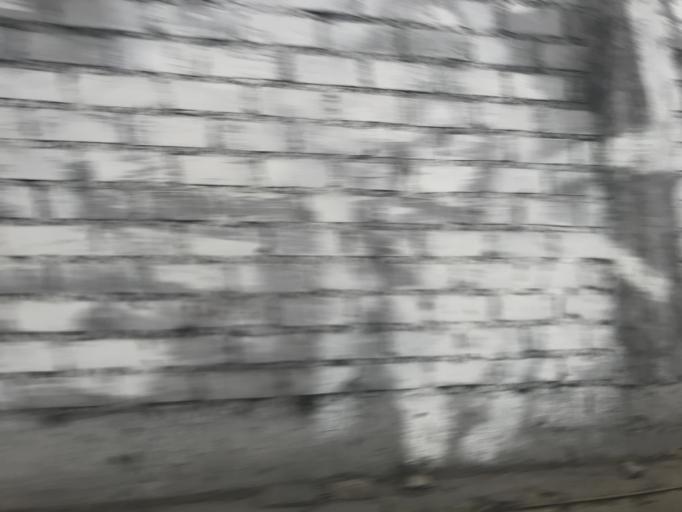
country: PE
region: Callao
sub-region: Callao
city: Callao
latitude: -12.0679
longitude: -77.0912
